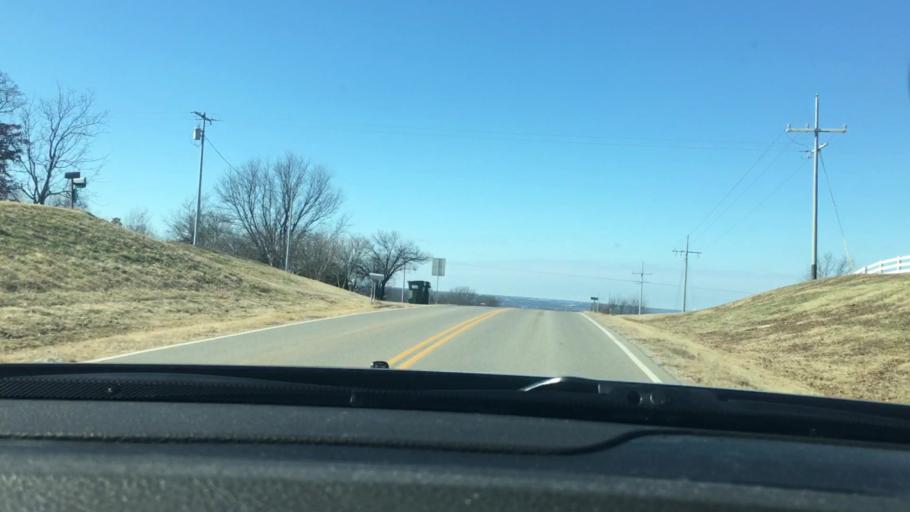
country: US
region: Oklahoma
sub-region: Murray County
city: Davis
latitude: 34.4771
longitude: -97.0540
